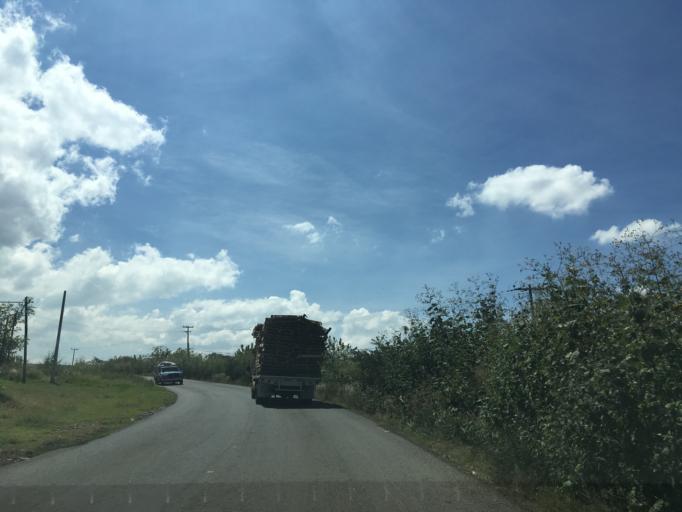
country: MX
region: Michoacan
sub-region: Morelia
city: La Mintzita (Piedra Dura)
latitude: 19.6660
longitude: -101.2833
